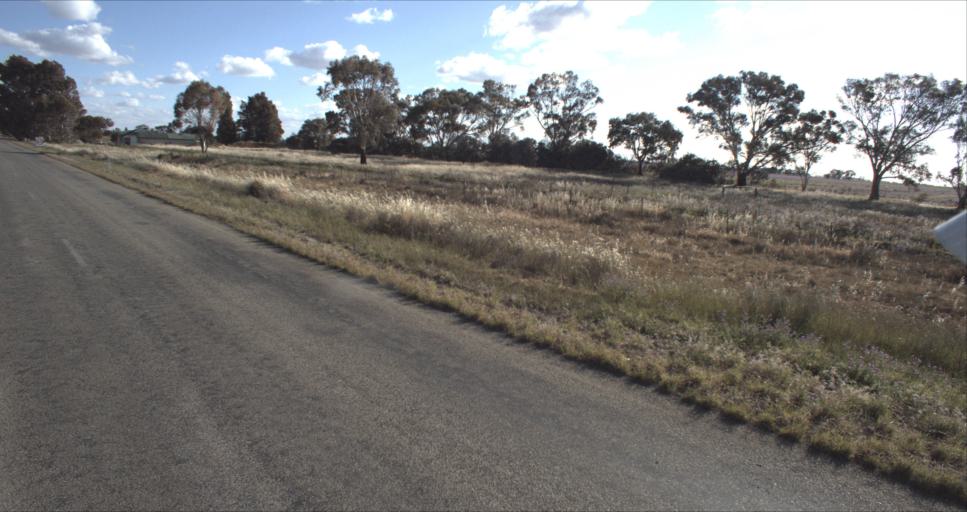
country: AU
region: New South Wales
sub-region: Leeton
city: Leeton
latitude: -34.5390
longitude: 146.2801
